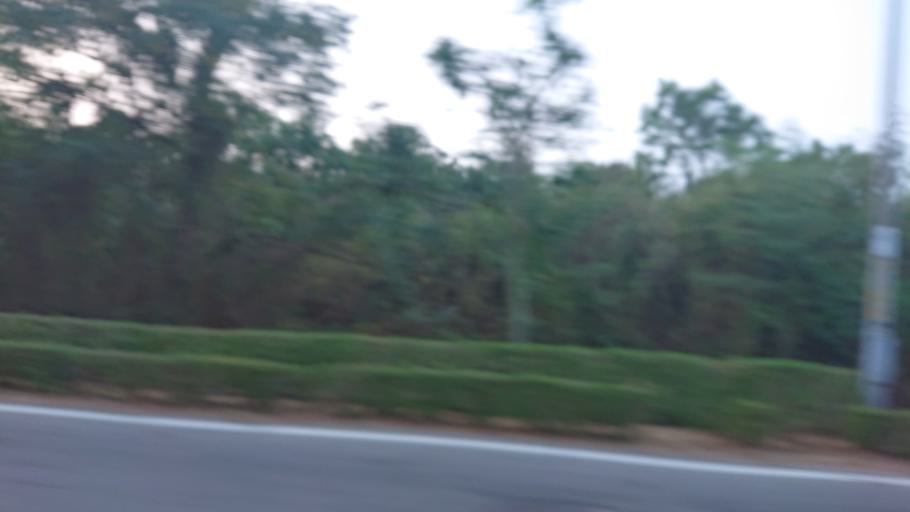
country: TW
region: Fukien
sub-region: Kinmen
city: Jincheng
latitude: 24.4570
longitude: 118.3207
